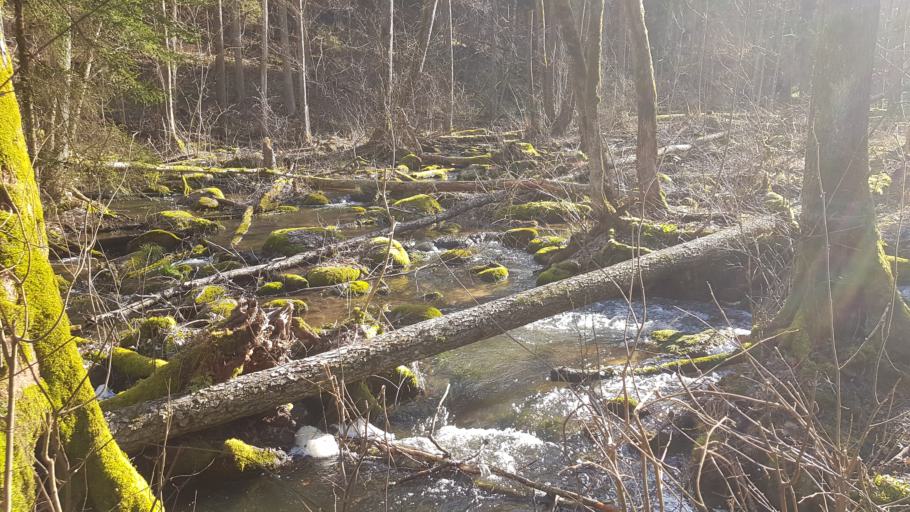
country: LT
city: Grigiskes
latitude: 54.7173
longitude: 25.0470
